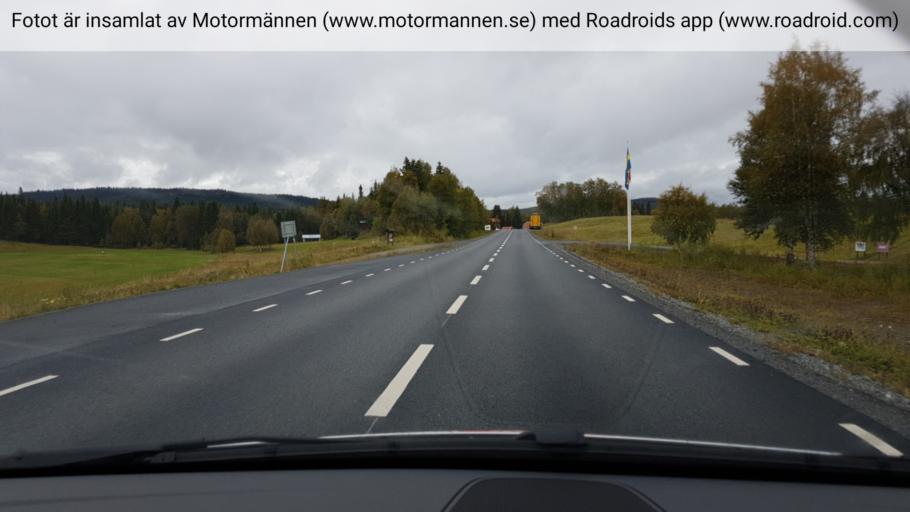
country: SE
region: Jaemtland
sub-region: Are Kommun
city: Are
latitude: 63.4034
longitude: 12.8168
